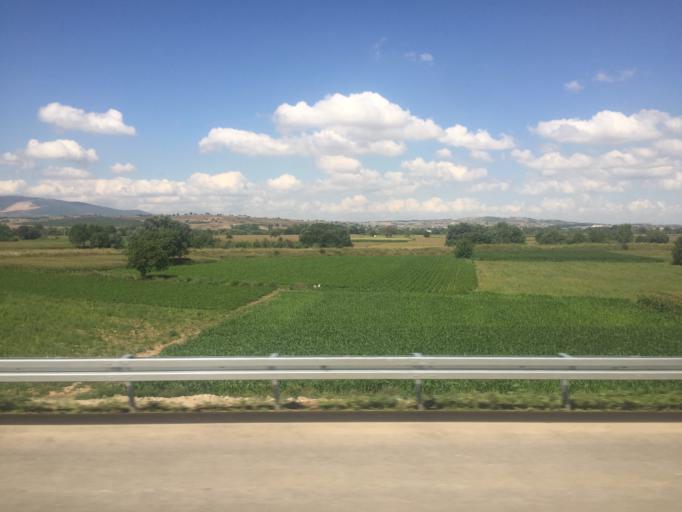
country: TR
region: Balikesir
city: Gobel
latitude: 40.0024
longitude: 28.1938
